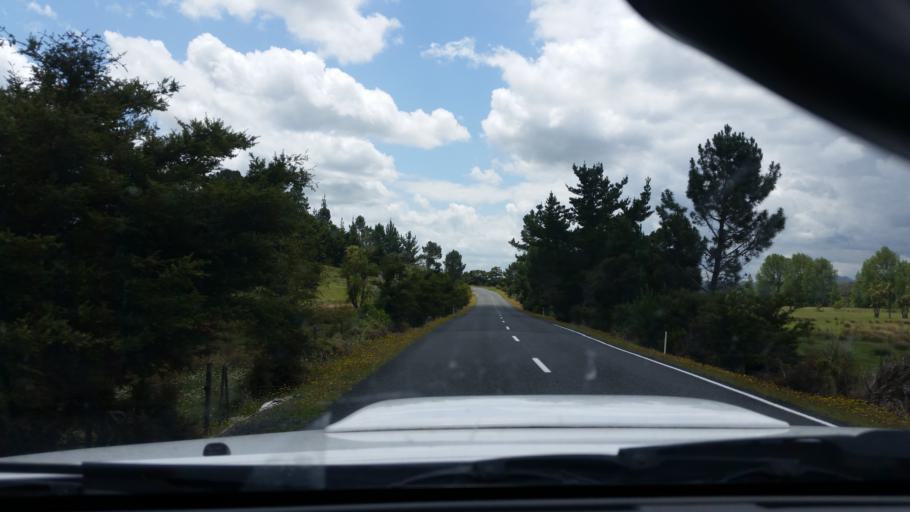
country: NZ
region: Northland
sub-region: Kaipara District
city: Dargaville
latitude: -35.8942
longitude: 173.8416
